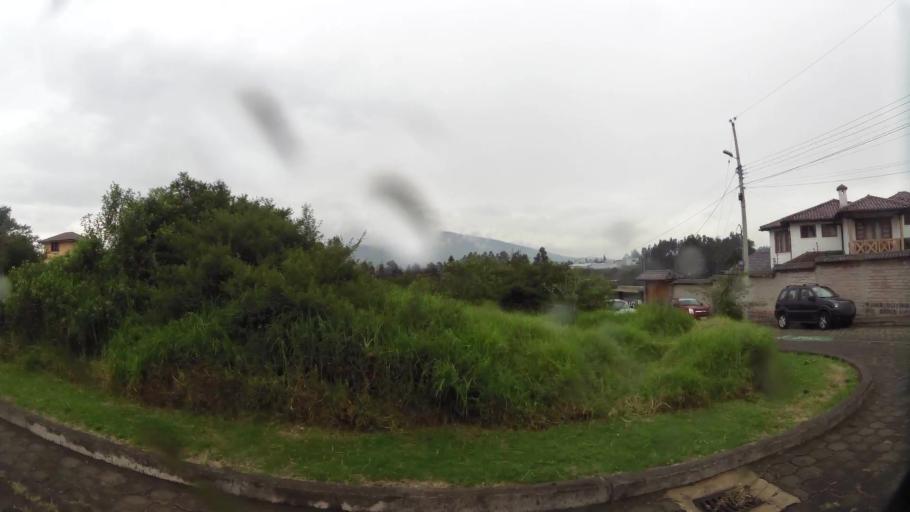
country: EC
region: Pichincha
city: Sangolqui
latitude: -0.3214
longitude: -78.4318
